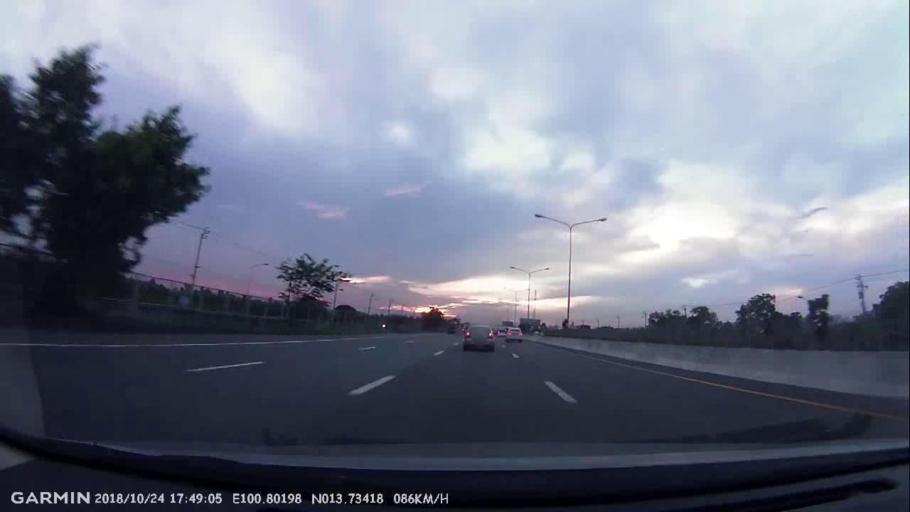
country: TH
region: Bangkok
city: Lat Krabang
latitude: 13.7340
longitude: 100.8016
